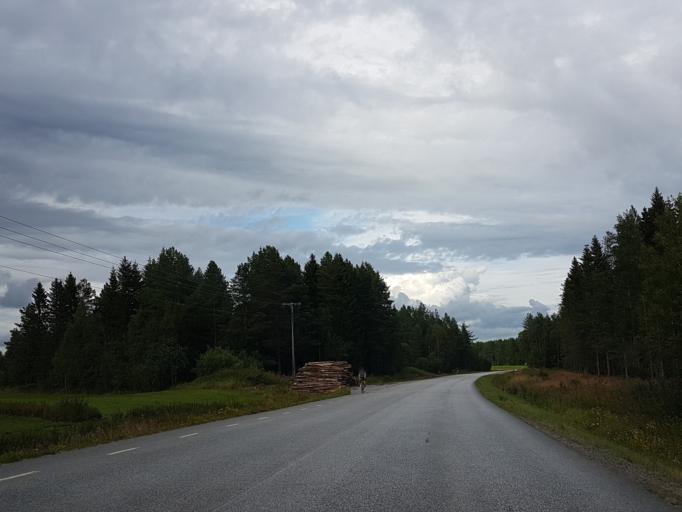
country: SE
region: Vaesterbotten
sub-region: Umea Kommun
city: Taftea
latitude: 63.8286
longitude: 20.4599
